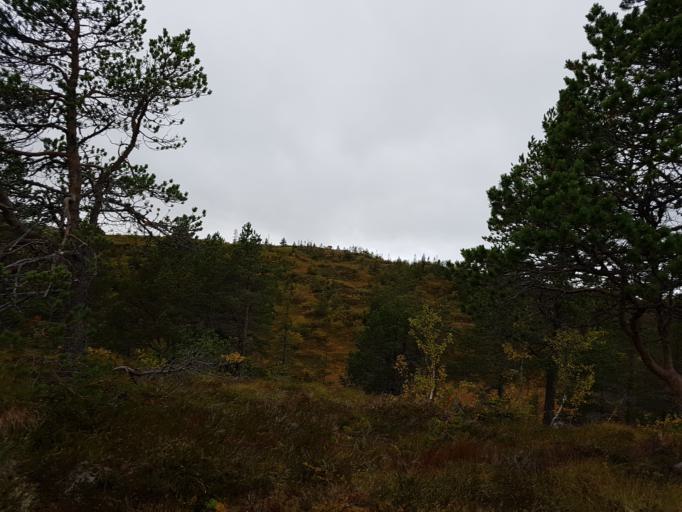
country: NO
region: Sor-Trondelag
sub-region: Melhus
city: Melhus
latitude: 63.4163
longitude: 10.2184
